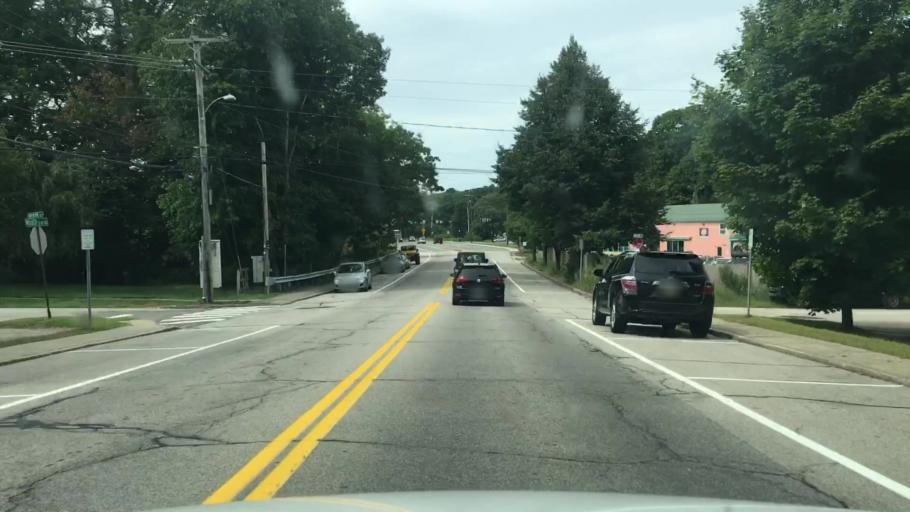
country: US
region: Maine
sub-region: York County
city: Kittery
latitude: 43.0868
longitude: -70.7467
